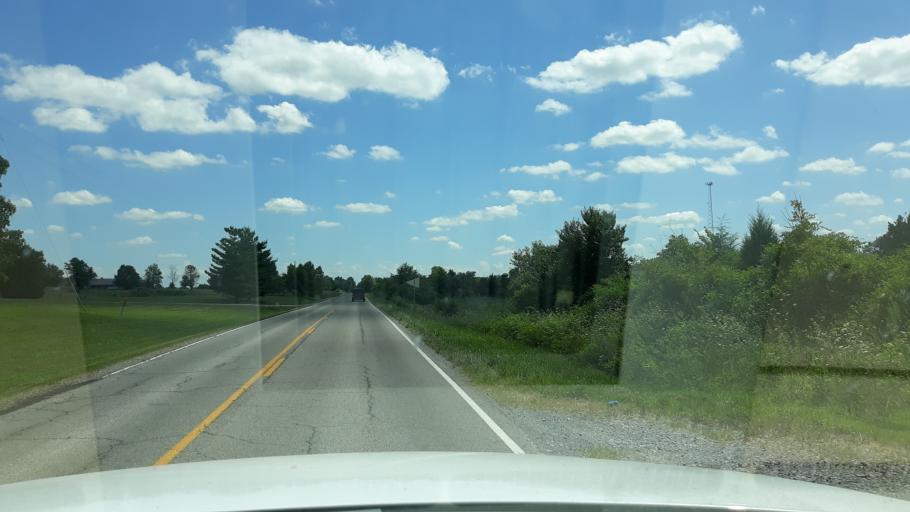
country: US
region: Illinois
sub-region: Saline County
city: Harrisburg
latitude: 37.8612
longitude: -88.6056
